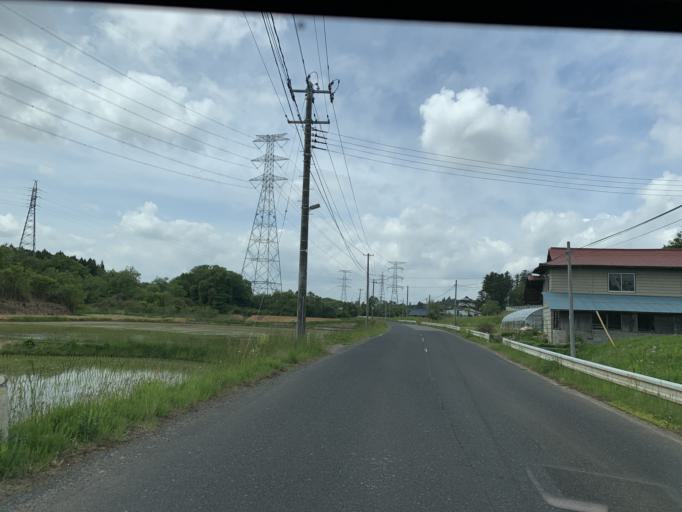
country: JP
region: Iwate
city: Ichinoseki
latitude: 38.8109
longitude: 141.0200
